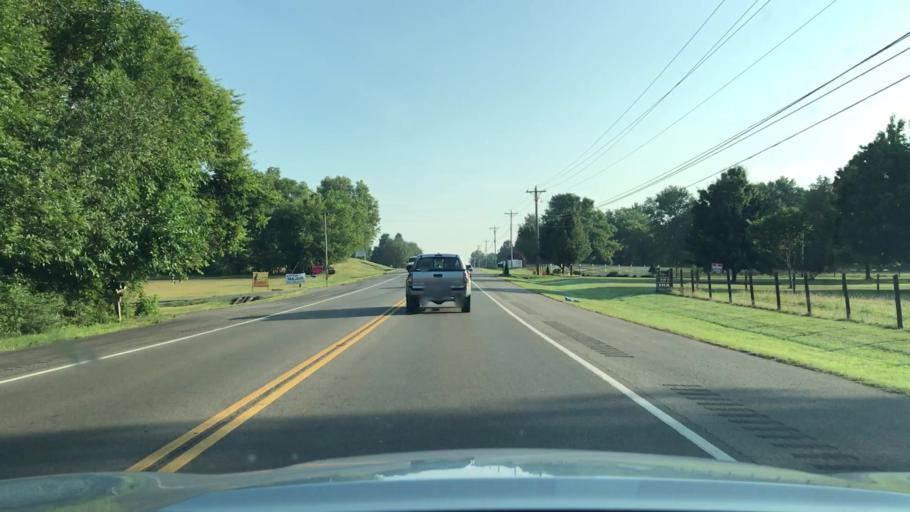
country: US
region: Tennessee
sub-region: Wilson County
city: Rural Hill
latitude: 36.1333
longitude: -86.5193
